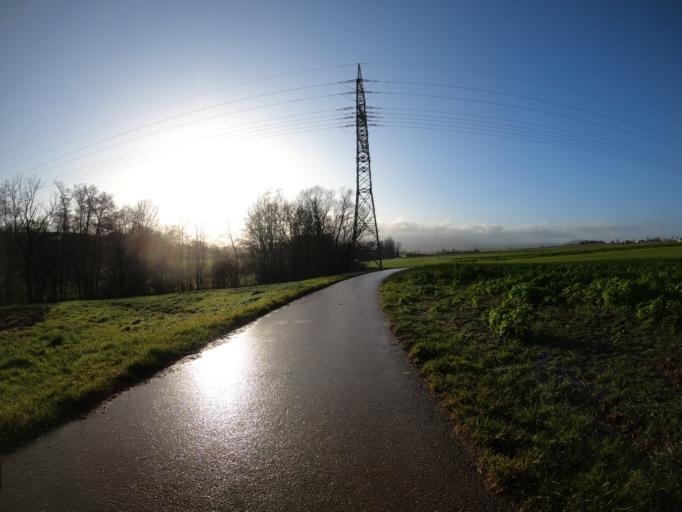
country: DE
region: Baden-Wuerttemberg
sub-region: Regierungsbezirk Stuttgart
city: Heiningen
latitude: 48.6756
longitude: 9.6254
